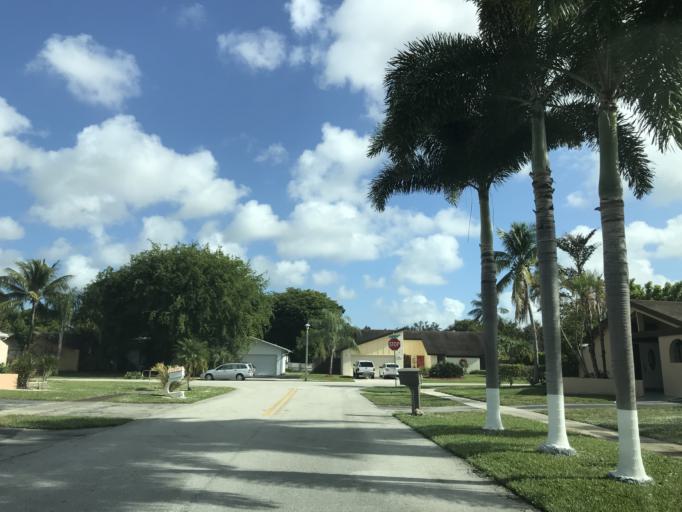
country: US
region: Florida
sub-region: Broward County
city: Coconut Creek
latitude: 26.2659
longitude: -80.1934
